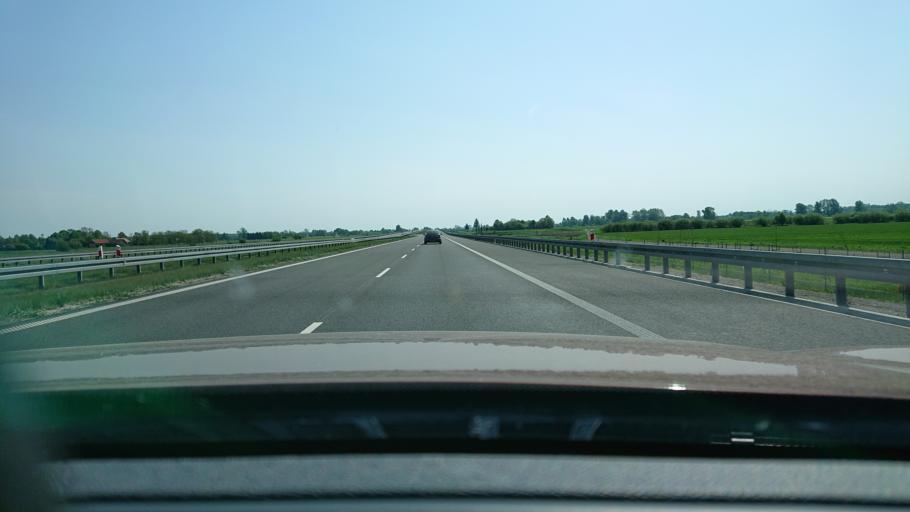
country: PL
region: Subcarpathian Voivodeship
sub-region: Powiat lancucki
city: Bialobrzegi
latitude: 50.1139
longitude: 22.3518
